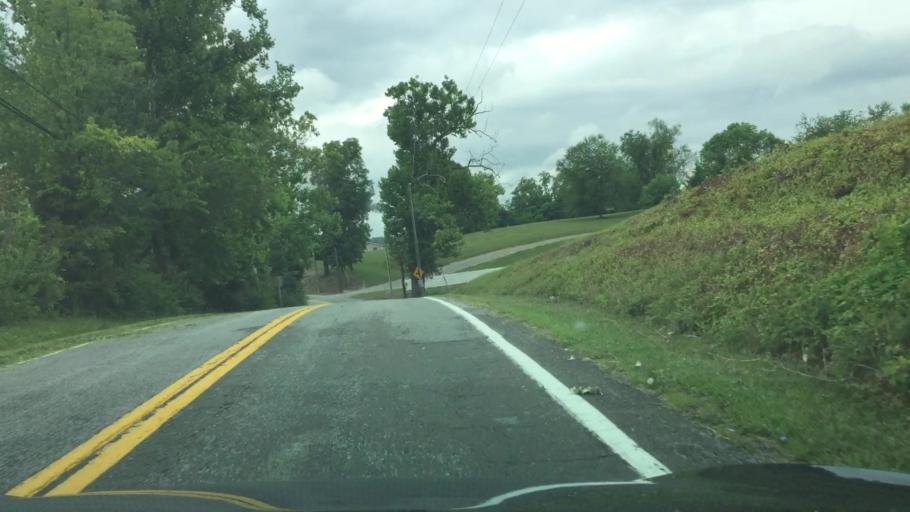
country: US
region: Virginia
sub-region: Pulaski County
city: Pulaski
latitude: 37.0068
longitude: -80.7458
